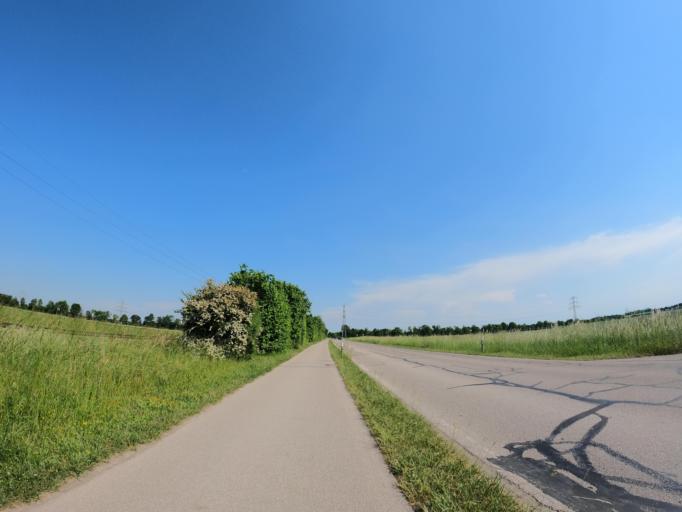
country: DE
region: Bavaria
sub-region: Upper Bavaria
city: Hohenbrunn
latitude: 48.0555
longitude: 11.6893
